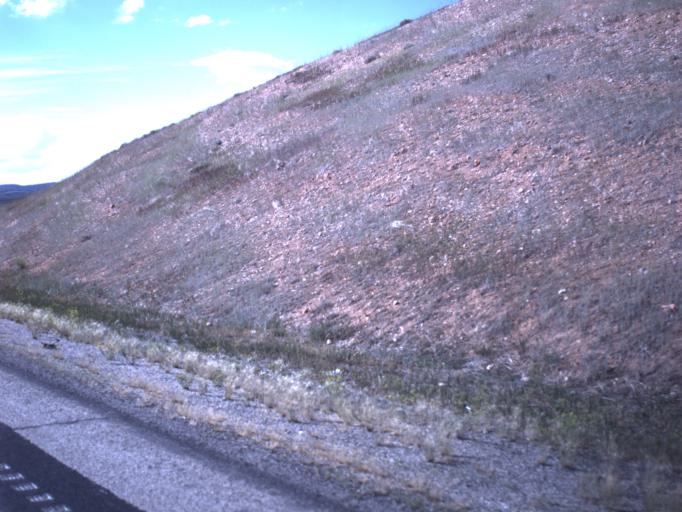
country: US
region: Utah
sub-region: Wasatch County
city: Heber
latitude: 40.2316
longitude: -111.1299
